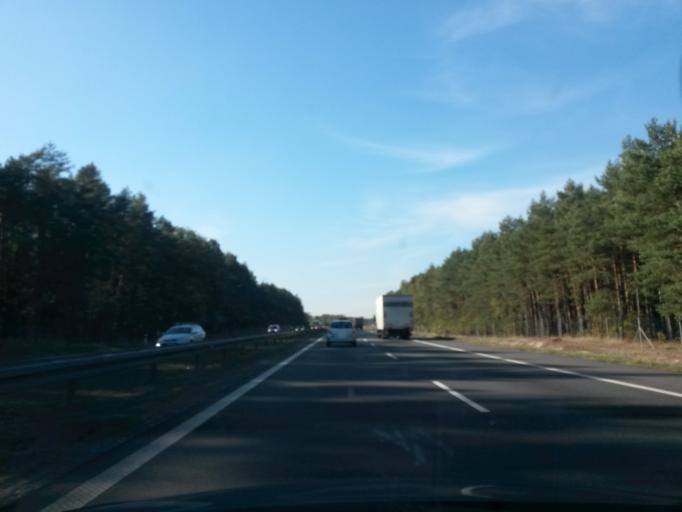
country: PL
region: Opole Voivodeship
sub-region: Powiat opolski
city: Komprachcice
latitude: 50.5861
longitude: 17.8196
